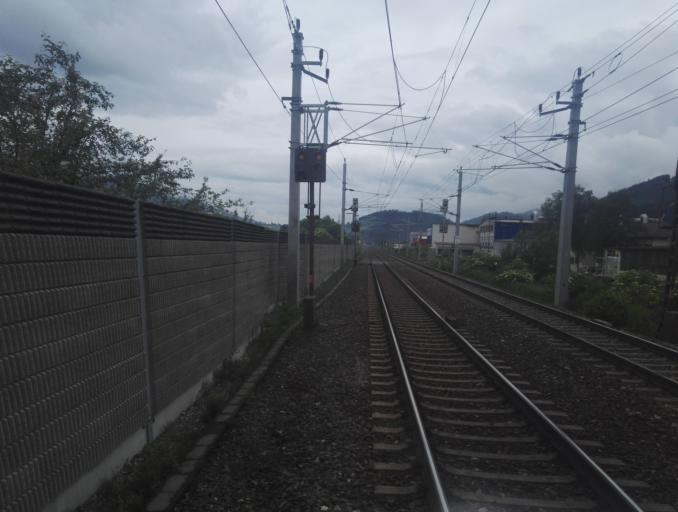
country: AT
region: Styria
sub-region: Politischer Bezirk Bruck-Muerzzuschlag
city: Mitterdorf im Muerztal
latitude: 47.5344
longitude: 15.5043
